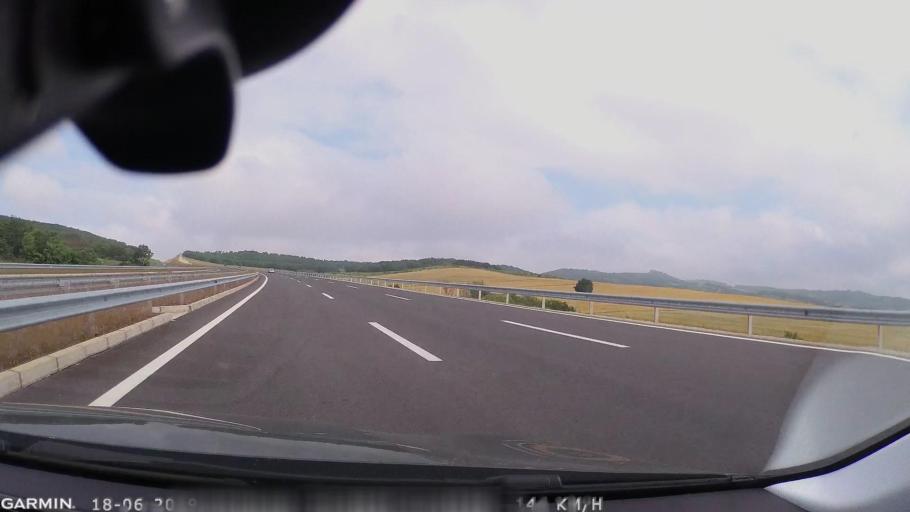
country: MK
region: Sveti Nikole
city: Gorobinci
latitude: 41.9187
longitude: 21.8739
